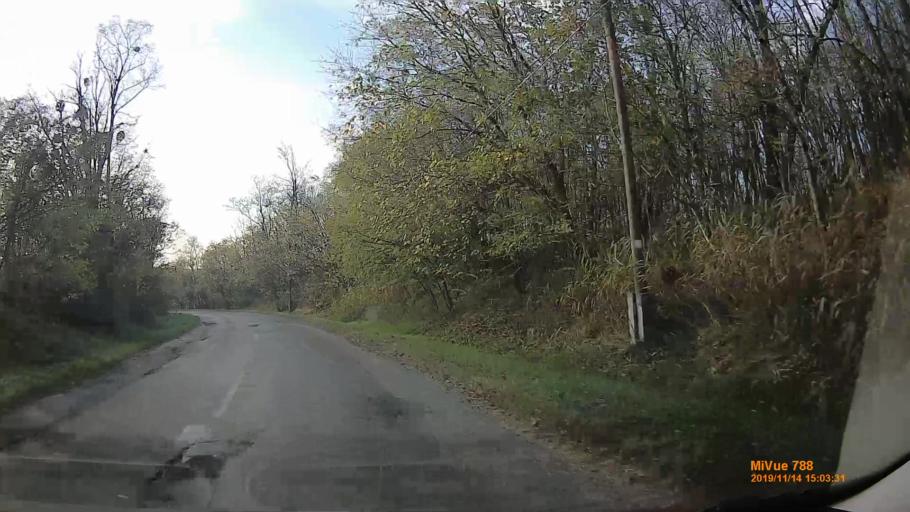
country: HU
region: Gyor-Moson-Sopron
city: Bakonyszentlaszlo
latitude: 47.4006
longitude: 17.8228
